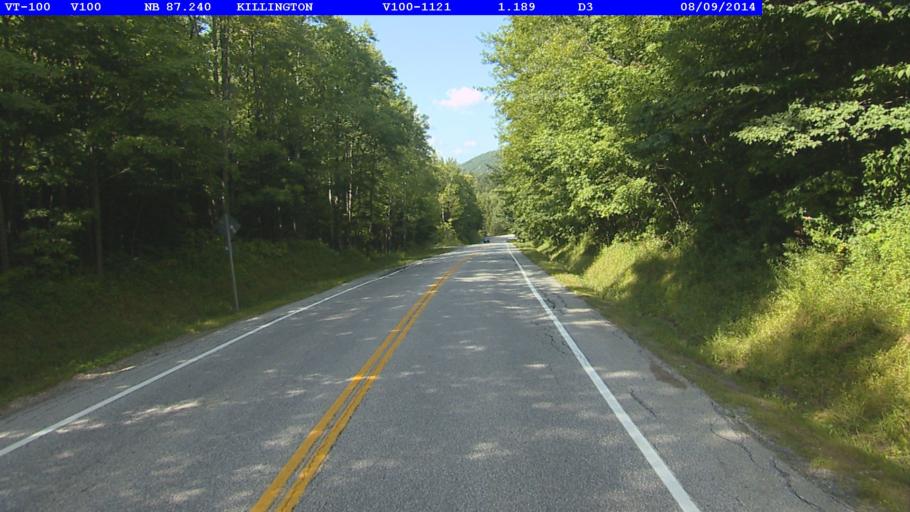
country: US
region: Vermont
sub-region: Rutland County
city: Rutland
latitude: 43.6831
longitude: -72.8135
